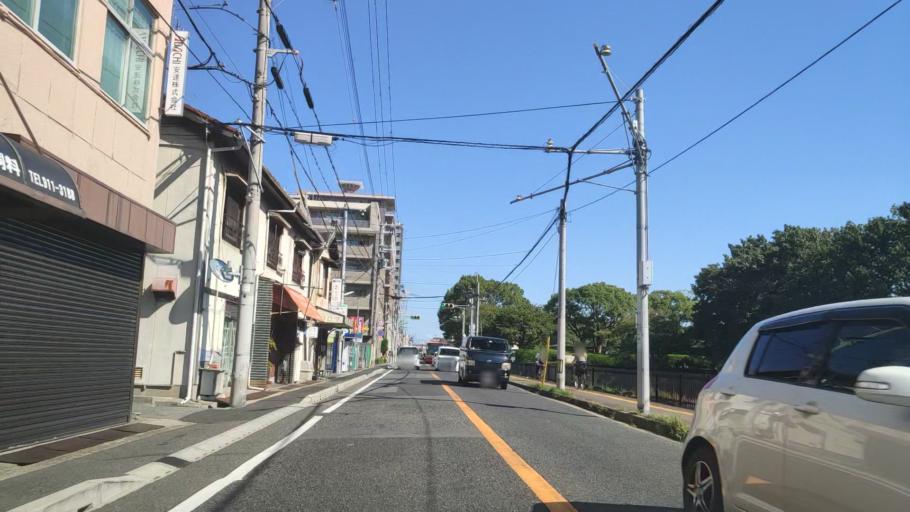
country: JP
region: Hyogo
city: Akashi
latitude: 34.6519
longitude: 134.9882
